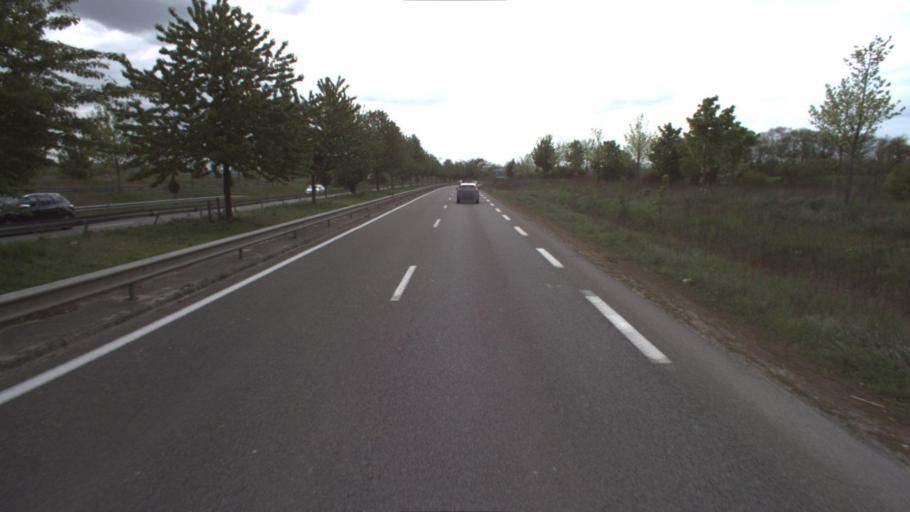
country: FR
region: Ile-de-France
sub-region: Departement de Seine-et-Marne
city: Villenoy
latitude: 48.9474
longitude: 2.8551
